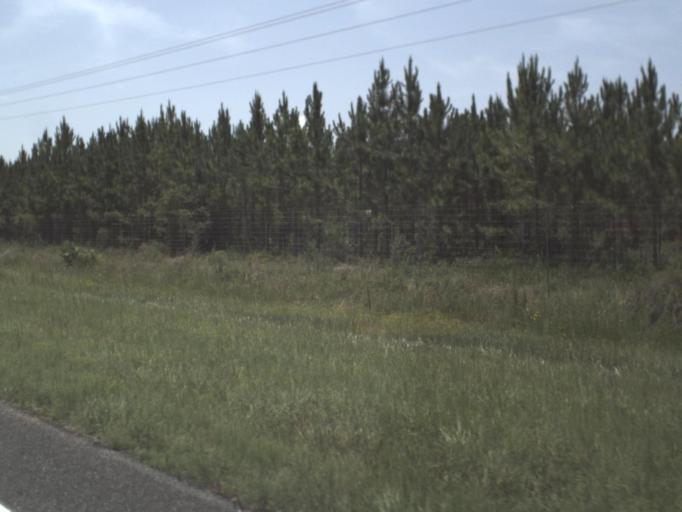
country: US
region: Florida
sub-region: Taylor County
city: Steinhatchee
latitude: 29.7927
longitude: -83.3345
